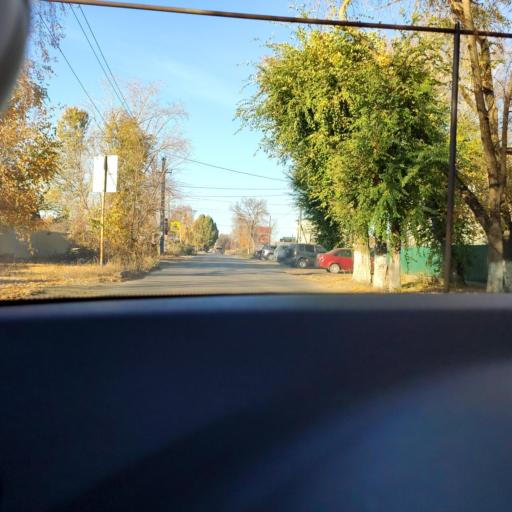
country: RU
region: Samara
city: Petra-Dubrava
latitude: 53.2491
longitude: 50.3283
